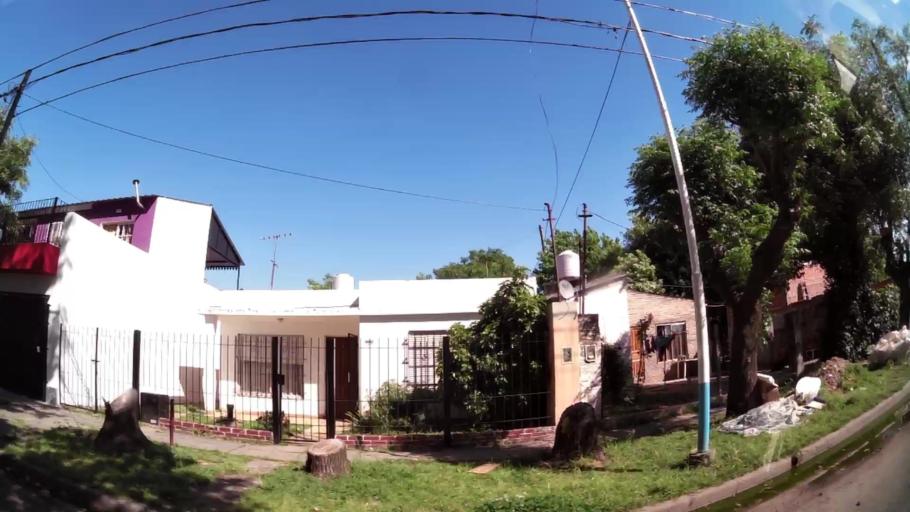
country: AR
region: Buenos Aires
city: Hurlingham
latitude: -34.4932
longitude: -58.6933
